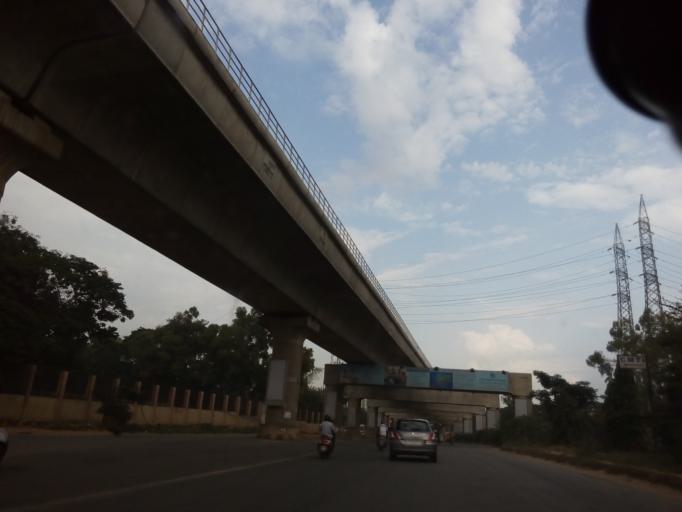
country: IN
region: Karnataka
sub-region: Bangalore Urban
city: Bangalore
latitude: 13.0314
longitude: 77.5356
